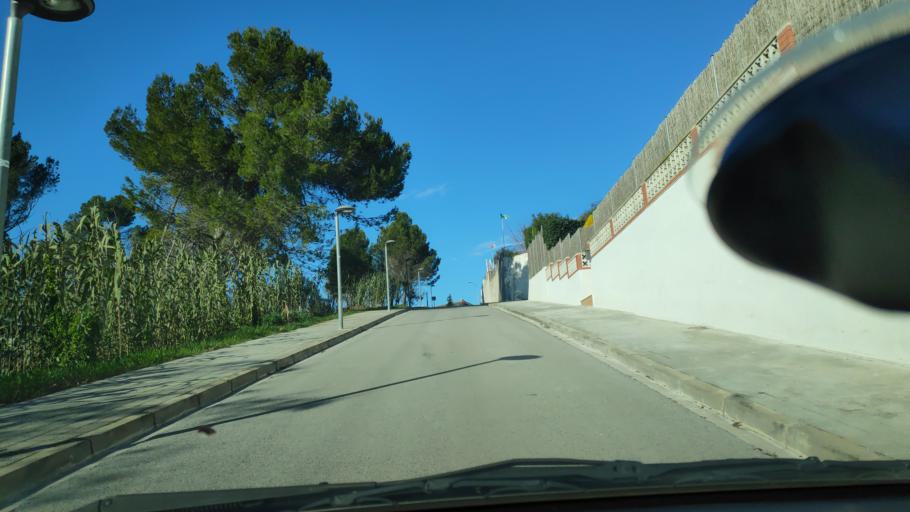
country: ES
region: Catalonia
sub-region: Provincia de Barcelona
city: Sant Quirze del Valles
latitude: 41.5226
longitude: 2.0725
